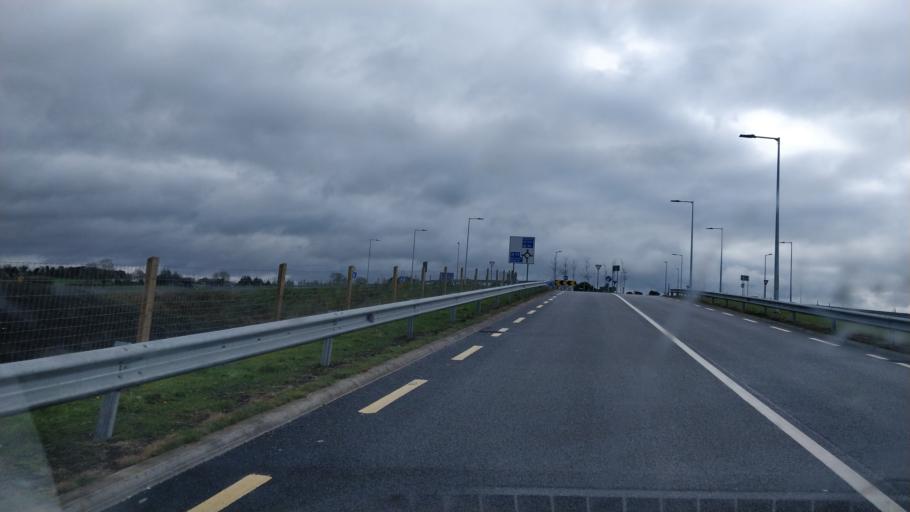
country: IE
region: Leinster
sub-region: An Iarmhi
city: Moate
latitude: 53.4010
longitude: -7.8297
